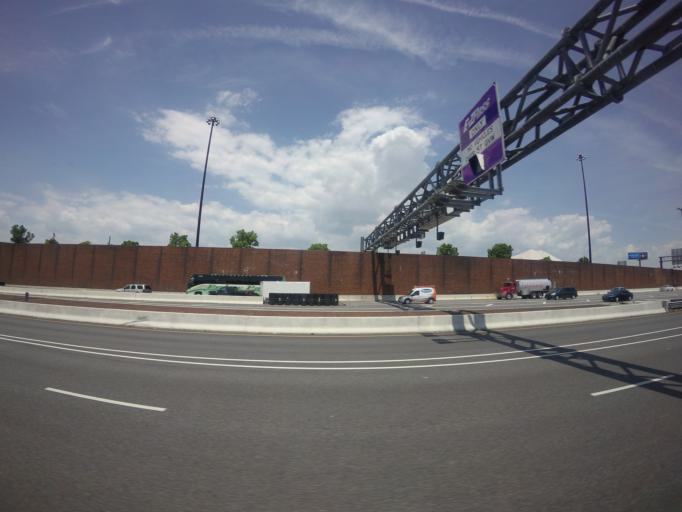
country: US
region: Maryland
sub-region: Baltimore County
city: Dundalk
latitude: 39.2644
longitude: -76.5652
